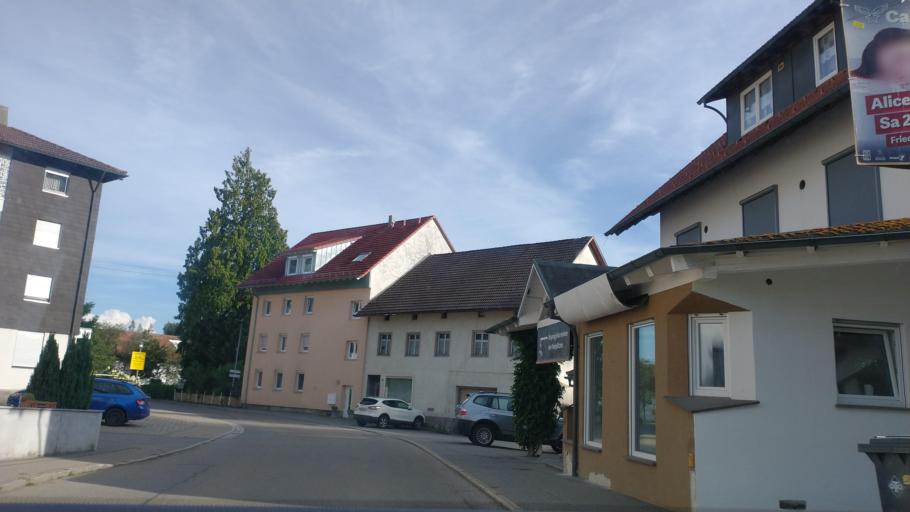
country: DE
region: Baden-Wuerttemberg
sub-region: Tuebingen Region
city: Neukirch
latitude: 47.6587
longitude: 9.7019
